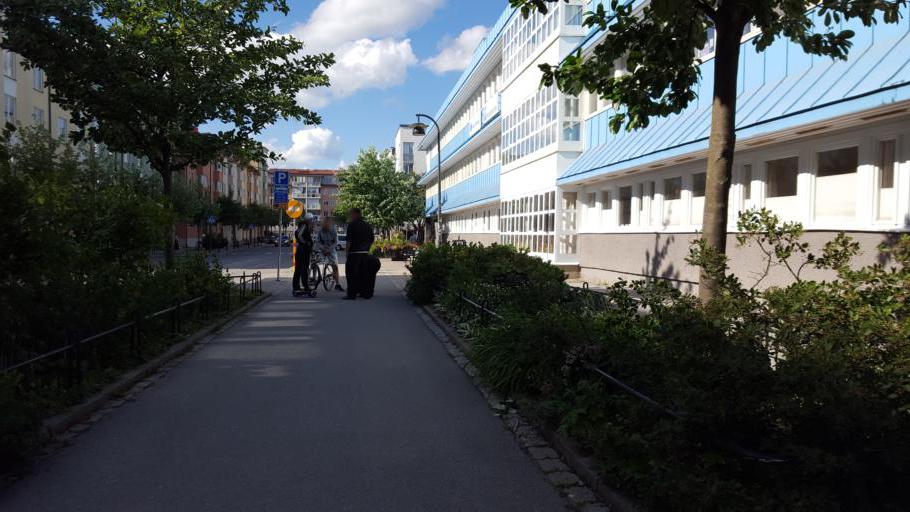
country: SE
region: Stockholm
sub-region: Upplands Vasby Kommun
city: Upplands Vaesby
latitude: 59.5192
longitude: 17.9095
